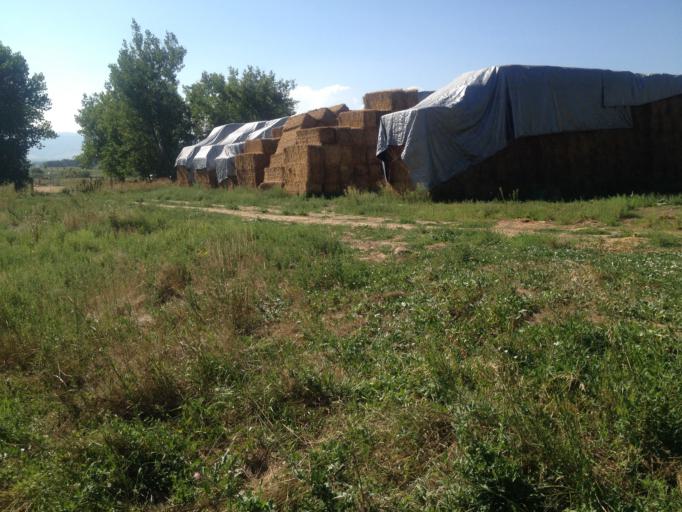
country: US
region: Colorado
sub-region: Boulder County
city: Gunbarrel
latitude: 40.0381
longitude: -105.1422
